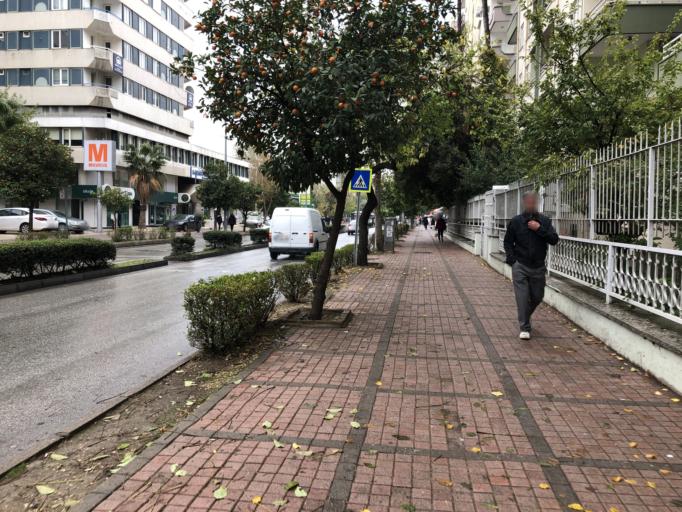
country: TR
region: Antalya
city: Antalya
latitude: 36.8935
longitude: 30.6934
